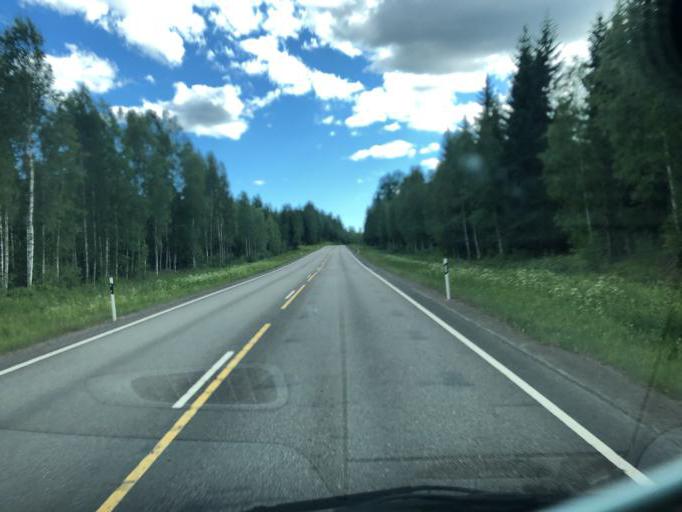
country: FI
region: Kymenlaakso
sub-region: Kouvola
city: Kouvola
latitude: 61.0116
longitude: 26.9503
